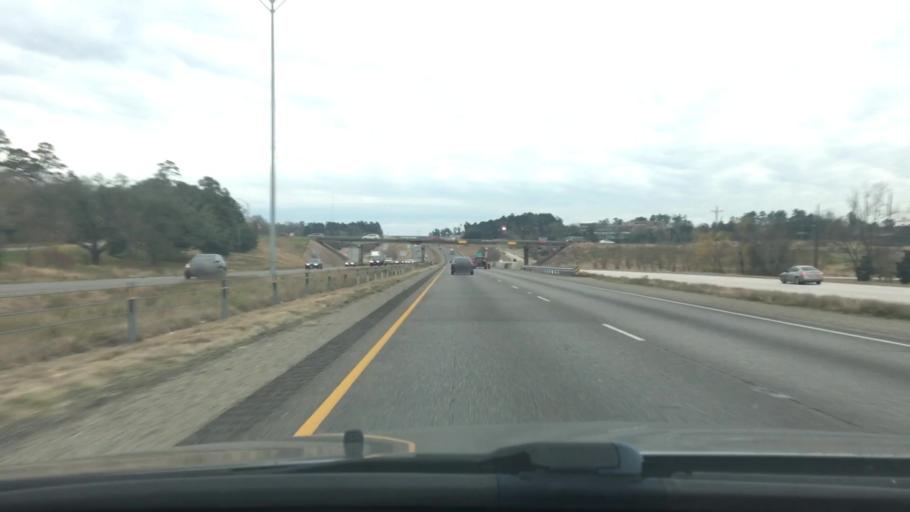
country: US
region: Texas
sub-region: Walker County
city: Huntsville
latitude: 30.7071
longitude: -95.5624
